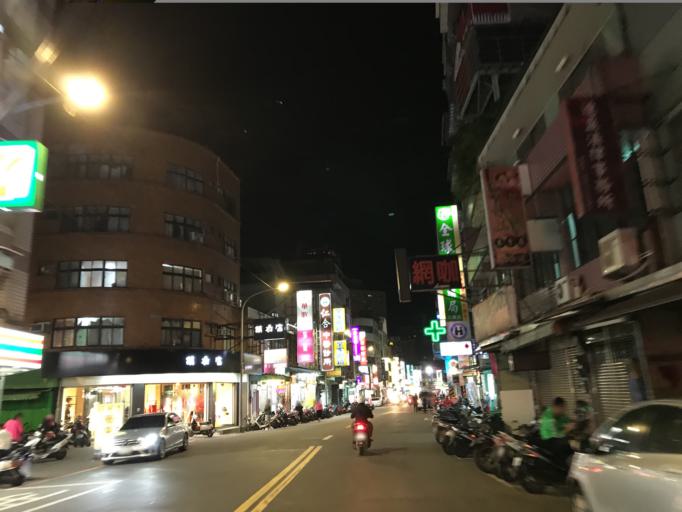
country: TW
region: Taiwan
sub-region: Taoyuan
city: Taoyuan
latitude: 24.9360
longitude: 121.3706
